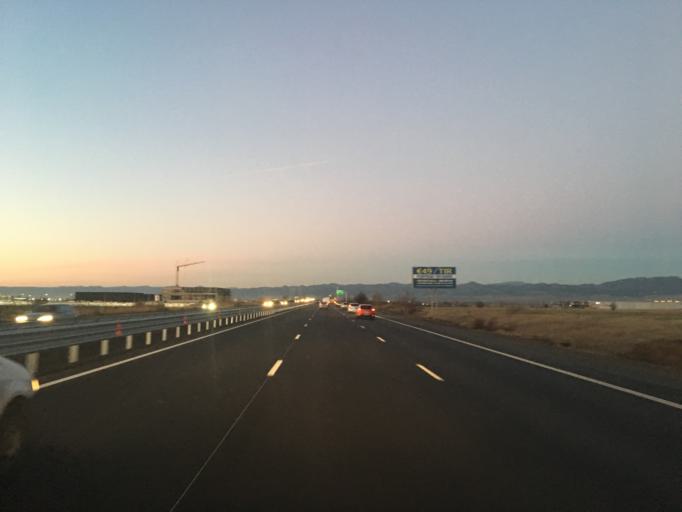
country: BG
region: Sofia-Capital
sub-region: Stolichna Obshtina
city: Sofia
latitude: 42.6999
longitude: 23.4511
